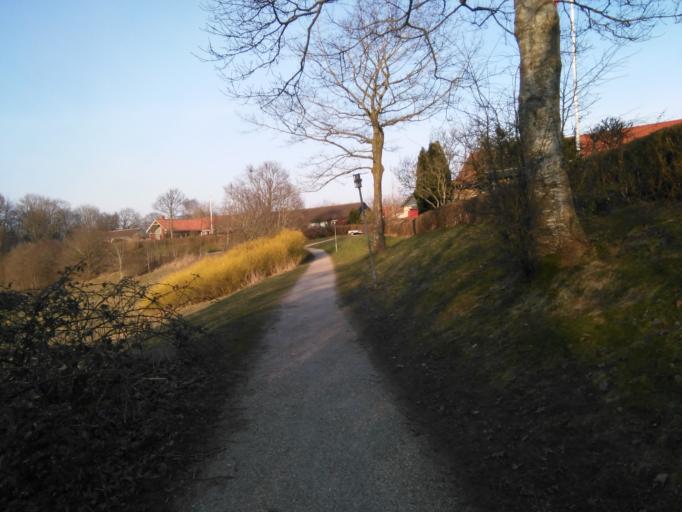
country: DK
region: Central Jutland
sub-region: Arhus Kommune
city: Beder
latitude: 56.0650
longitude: 10.2088
